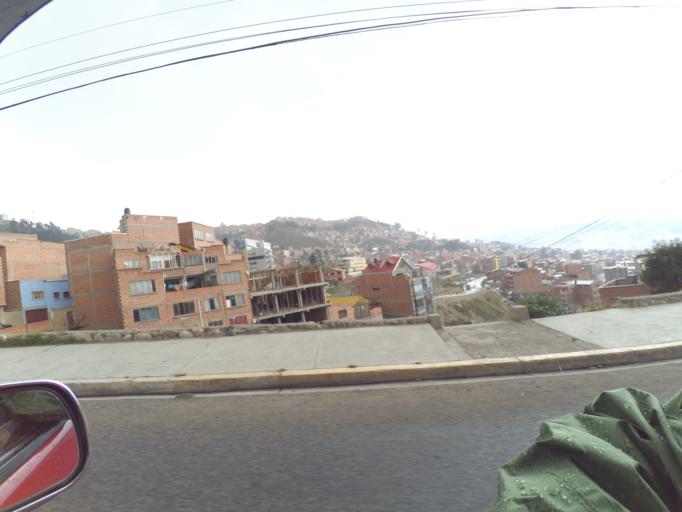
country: BO
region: La Paz
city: La Paz
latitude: -16.4915
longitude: -68.1660
